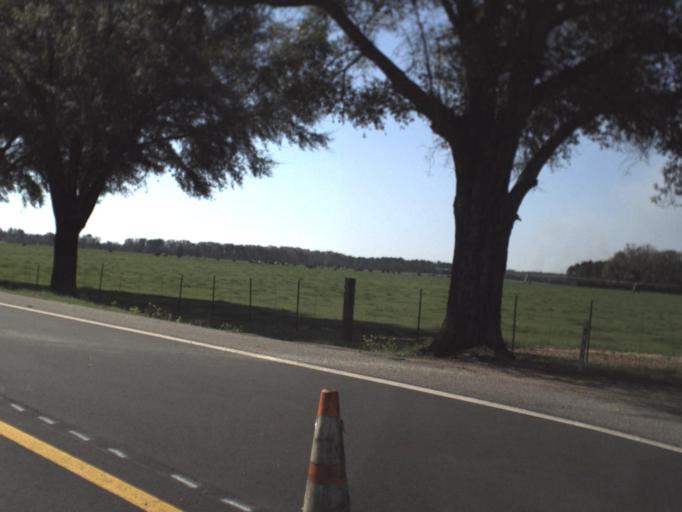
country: US
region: Florida
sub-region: Jackson County
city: Marianna
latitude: 30.7021
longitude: -85.1847
